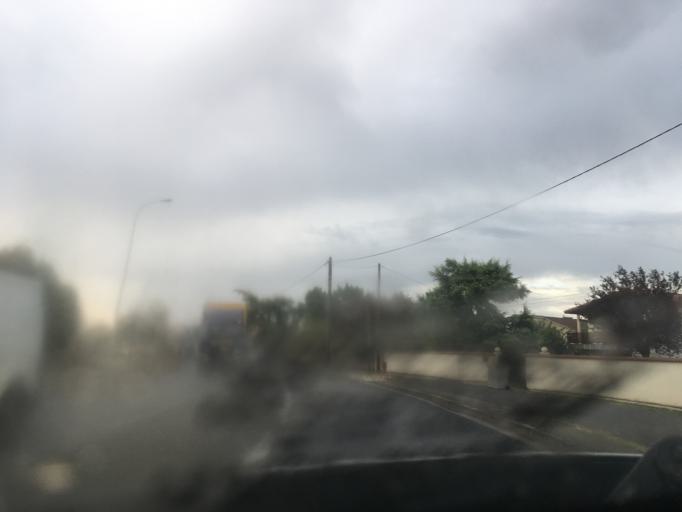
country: FR
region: Midi-Pyrenees
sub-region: Departement de la Haute-Garonne
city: Cugnaux
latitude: 43.5613
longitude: 1.3428
